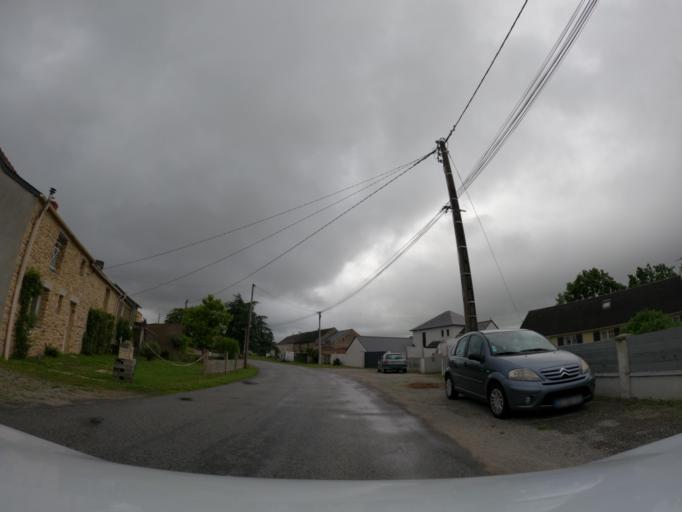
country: FR
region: Pays de la Loire
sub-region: Departement de la Loire-Atlantique
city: Saint-Mars-du-Desert
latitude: 47.3745
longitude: -1.4132
